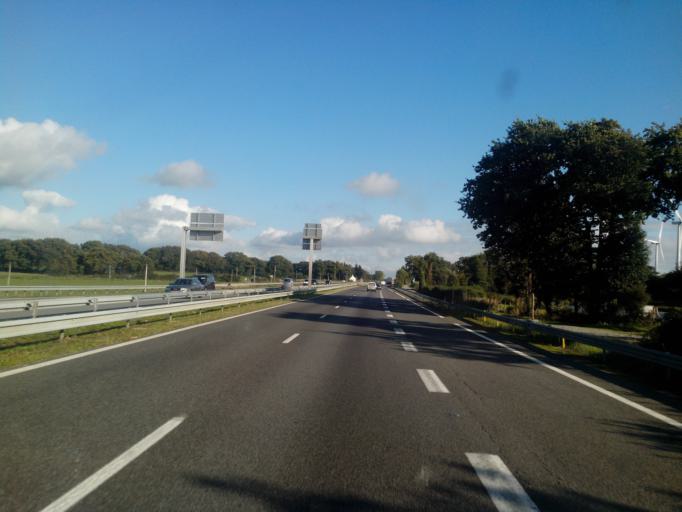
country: FR
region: Brittany
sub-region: Departement du Morbihan
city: Ambon
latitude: 47.5884
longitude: -2.5481
